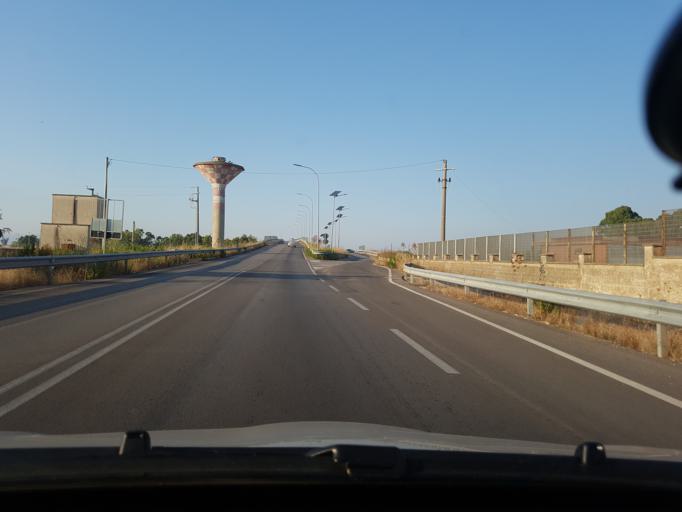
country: IT
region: Apulia
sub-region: Provincia di Foggia
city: Carapelle
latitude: 41.4039
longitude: 15.6511
